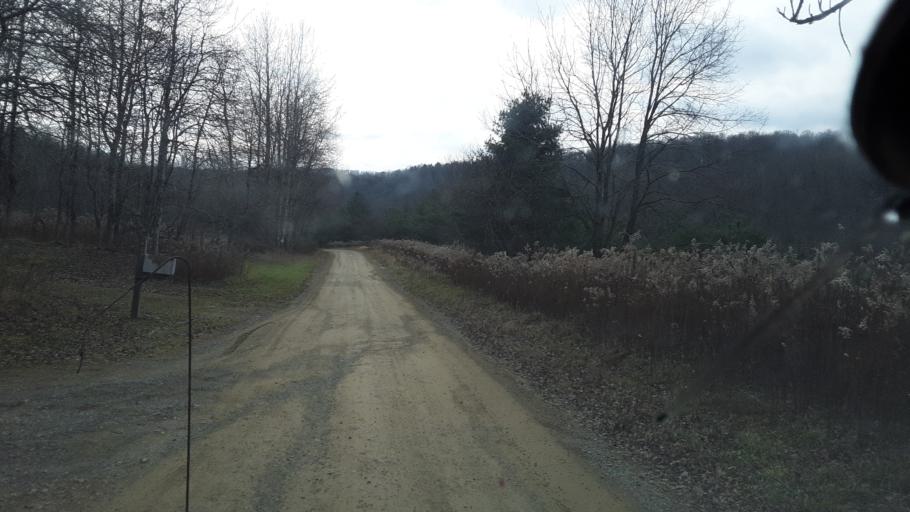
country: US
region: Pennsylvania
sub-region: Tioga County
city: Westfield
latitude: 41.9128
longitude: -77.7189
